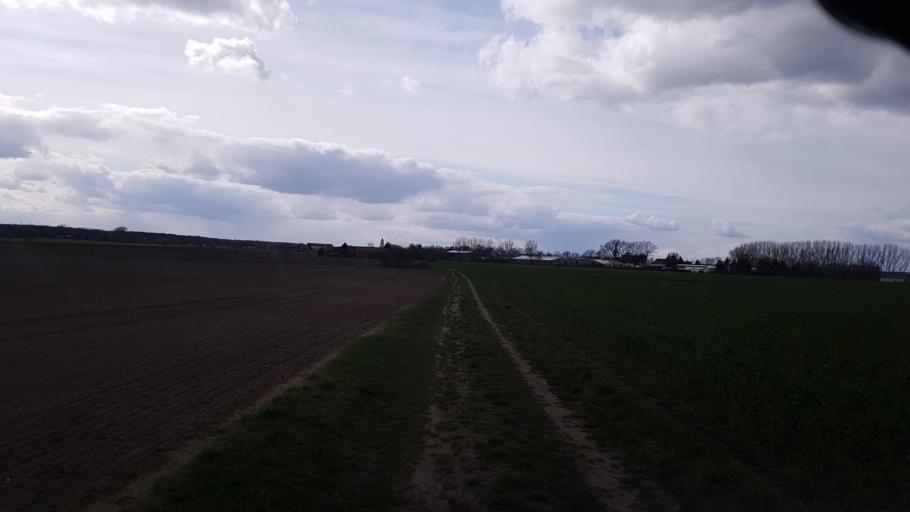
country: DE
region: Brandenburg
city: Hohenbucko
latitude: 51.6966
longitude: 13.4885
